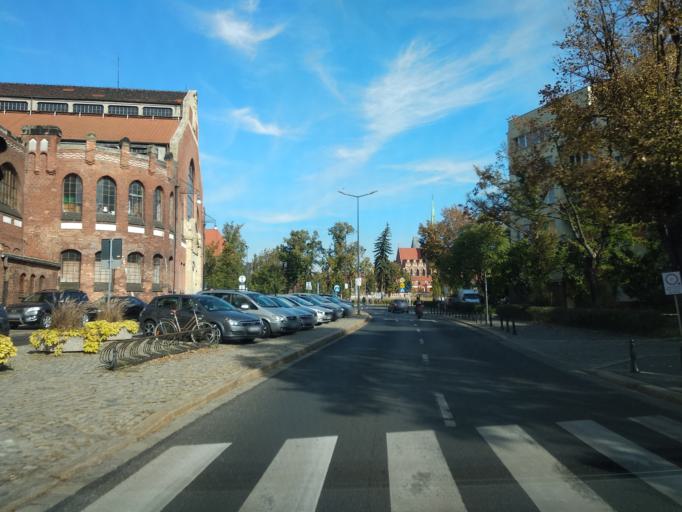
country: PL
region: Lower Silesian Voivodeship
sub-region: Powiat wroclawski
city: Wroclaw
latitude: 51.1119
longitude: 17.0408
